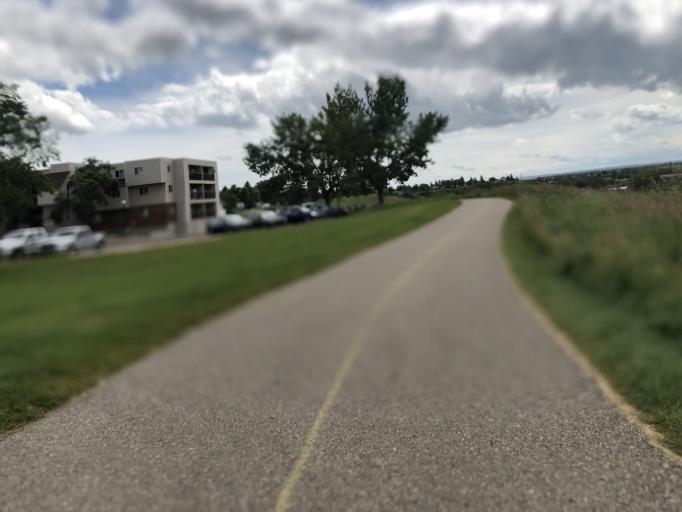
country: CA
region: Alberta
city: Calgary
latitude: 50.9949
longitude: -114.0230
